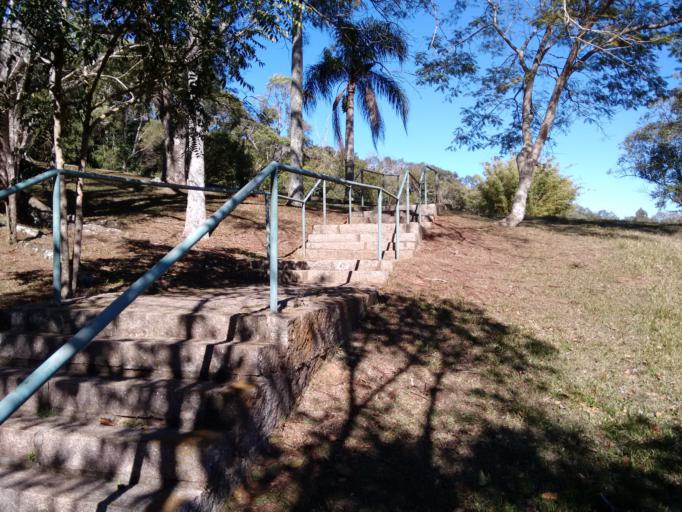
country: BR
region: Parana
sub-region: Ponta Grossa
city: Ponta Grossa
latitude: -25.2235
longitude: -50.0400
